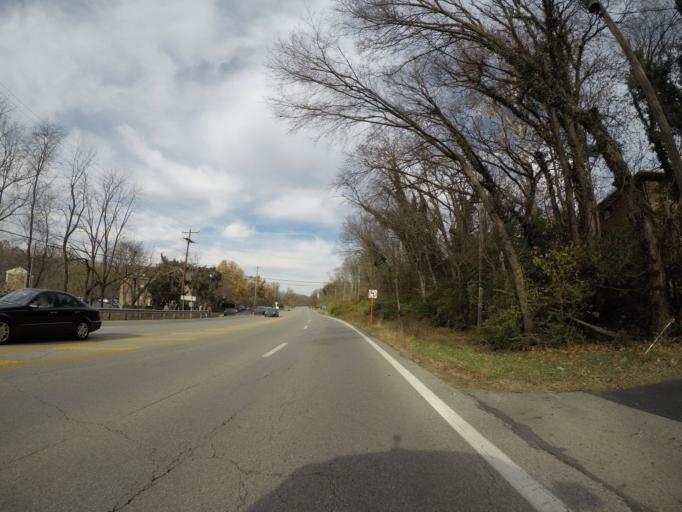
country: US
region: Ohio
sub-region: Franklin County
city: Upper Arlington
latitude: 40.0059
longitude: -83.0817
